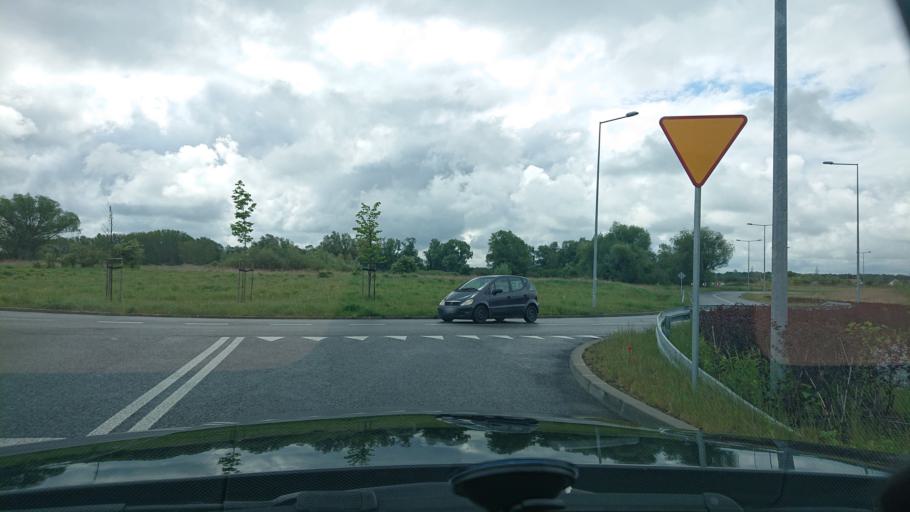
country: PL
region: Greater Poland Voivodeship
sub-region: Powiat gnieznienski
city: Gniezno
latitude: 52.5253
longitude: 17.6235
